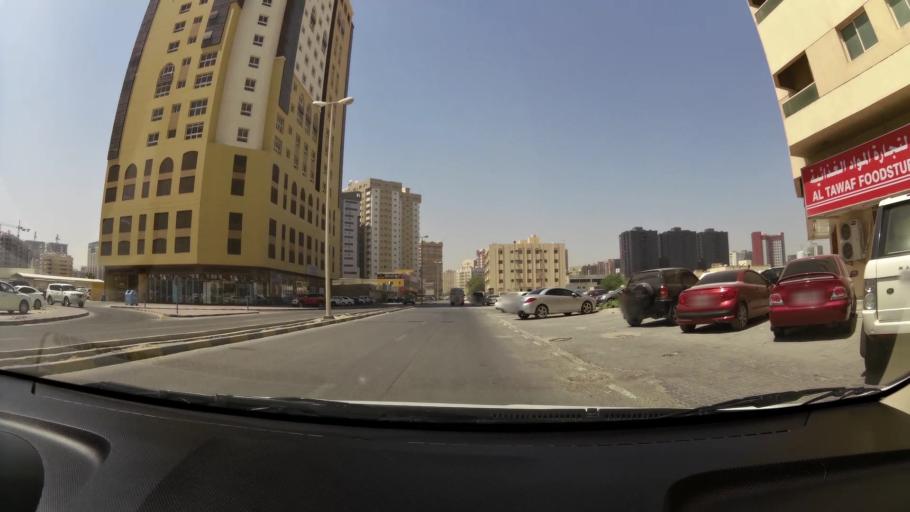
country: AE
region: Ajman
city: Ajman
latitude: 25.3926
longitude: 55.4661
